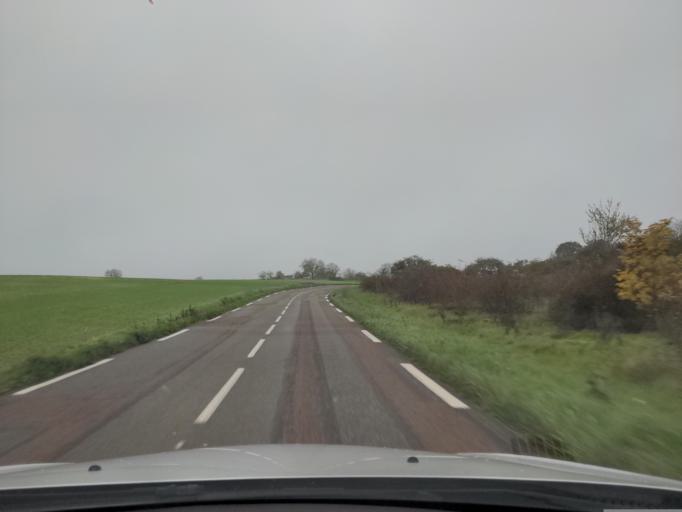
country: FR
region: Bourgogne
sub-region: Departement de la Cote-d'Or
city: Ruffey-les-Echirey
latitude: 47.3716
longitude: 5.0709
